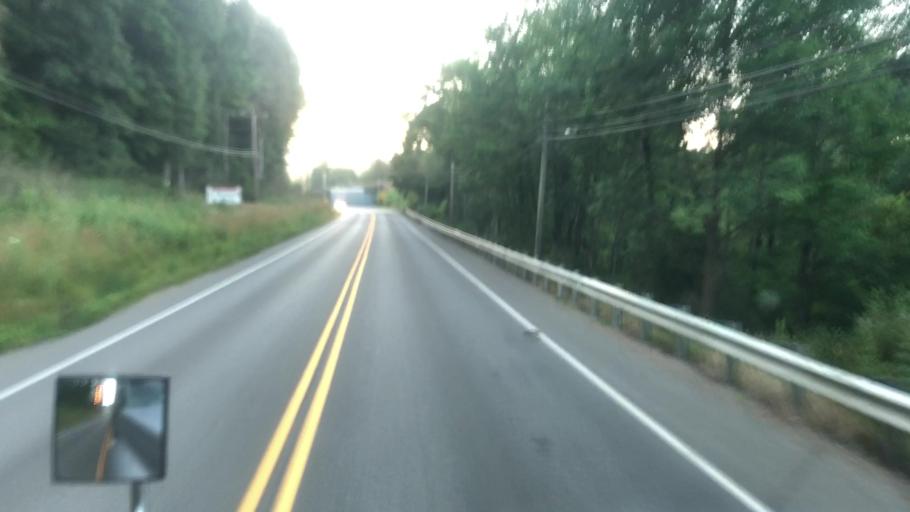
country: US
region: Pennsylvania
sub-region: Crawford County
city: Titusville
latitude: 41.6232
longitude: -79.6474
